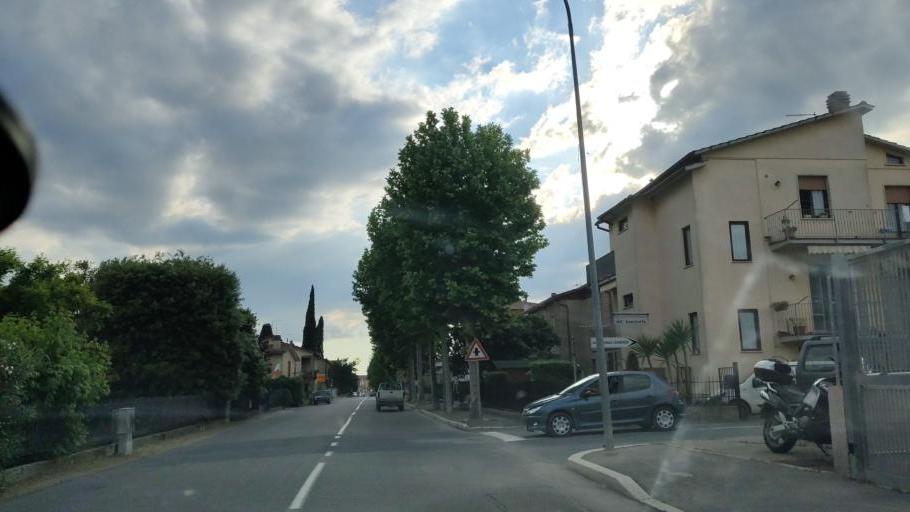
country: IT
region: Umbria
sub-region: Provincia di Terni
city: Giove
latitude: 42.5107
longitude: 12.3338
